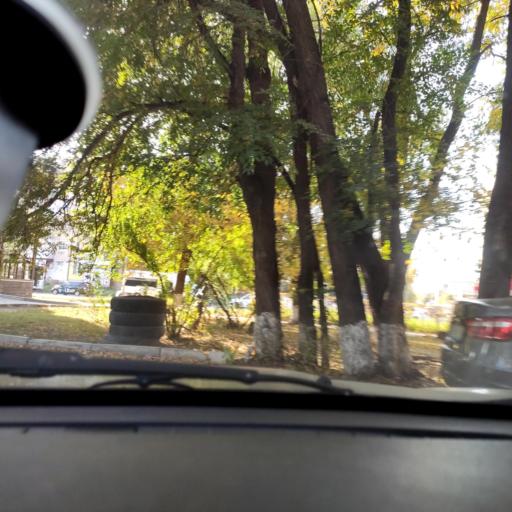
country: RU
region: Samara
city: Tol'yatti
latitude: 53.5234
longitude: 49.4151
